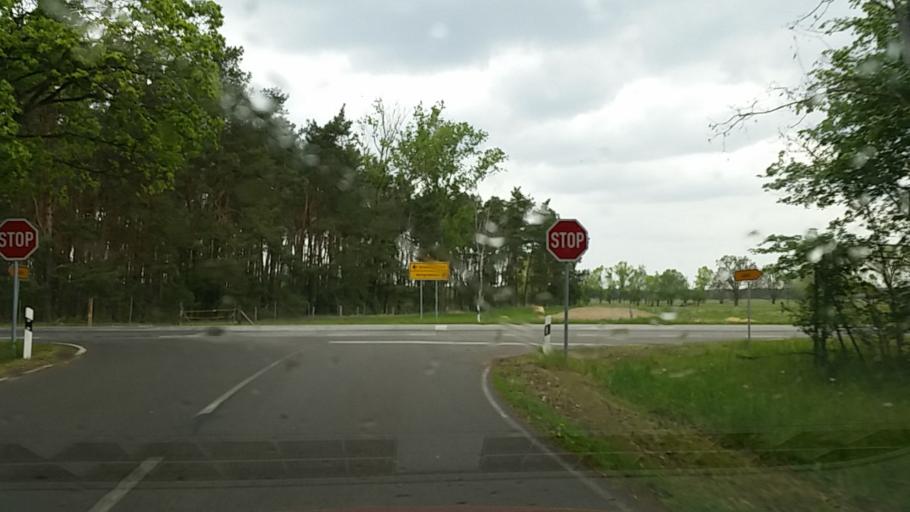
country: DE
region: Brandenburg
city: Storkow
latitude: 52.3253
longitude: 13.9403
